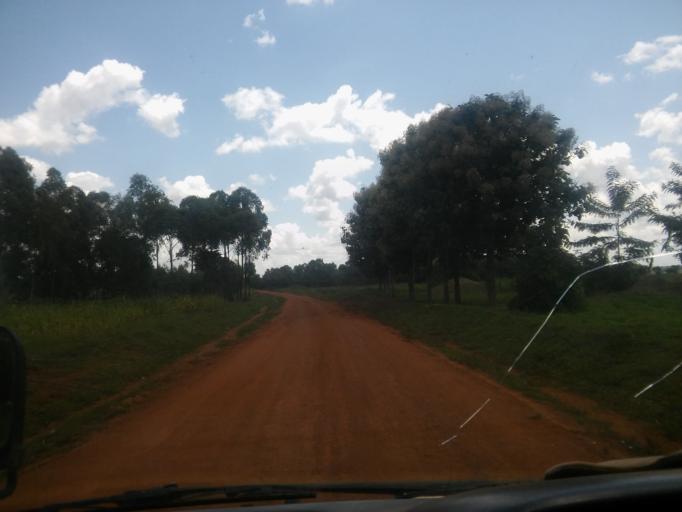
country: UG
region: Eastern Region
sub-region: Budaka District
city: Budaka
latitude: 1.1109
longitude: 33.9637
